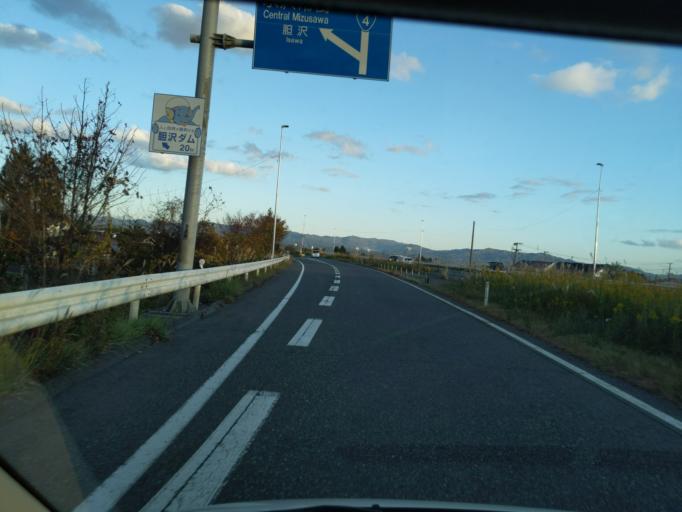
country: JP
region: Iwate
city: Mizusawa
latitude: 39.1690
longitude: 141.1280
